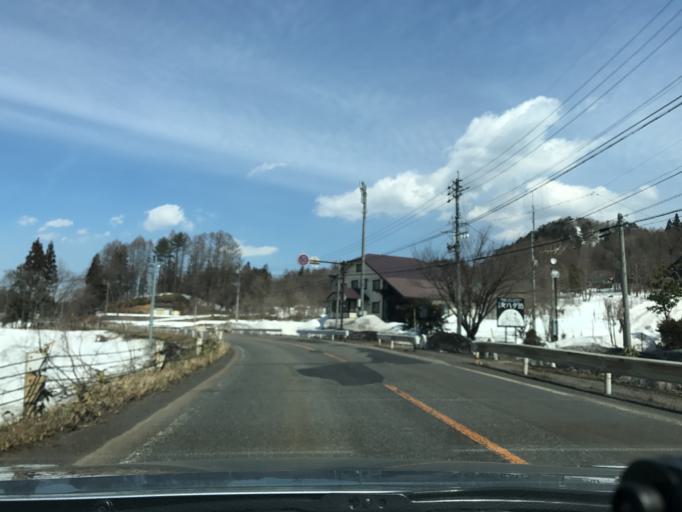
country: JP
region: Nagano
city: Omachi
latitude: 36.5945
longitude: 137.8457
